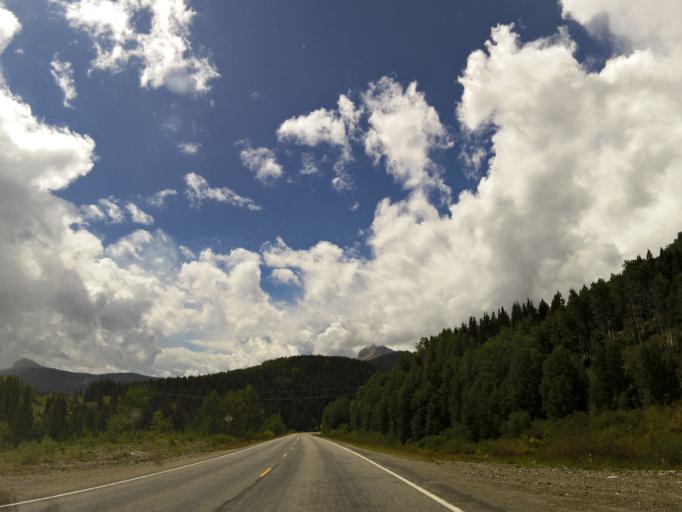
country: US
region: Colorado
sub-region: San Juan County
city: Silverton
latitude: 37.7282
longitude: -107.7324
